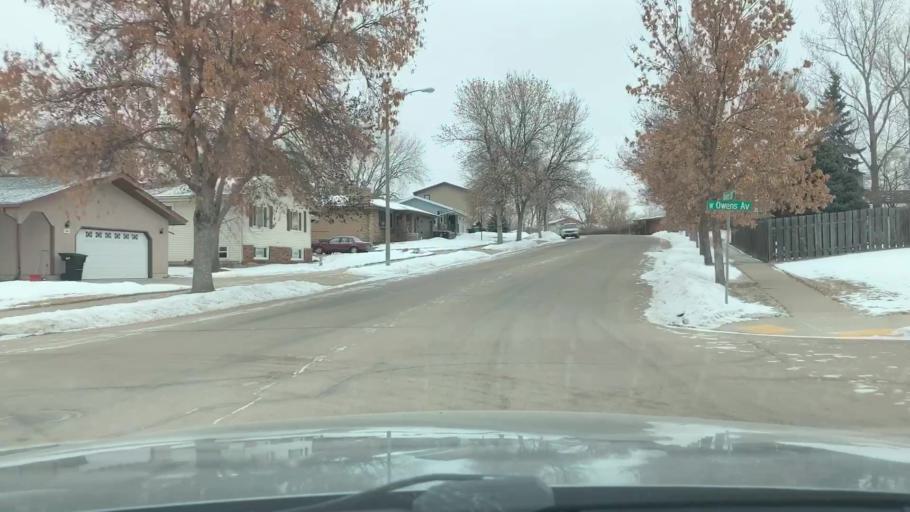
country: US
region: North Dakota
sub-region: Burleigh County
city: Bismarck
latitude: 46.8245
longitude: -100.8074
